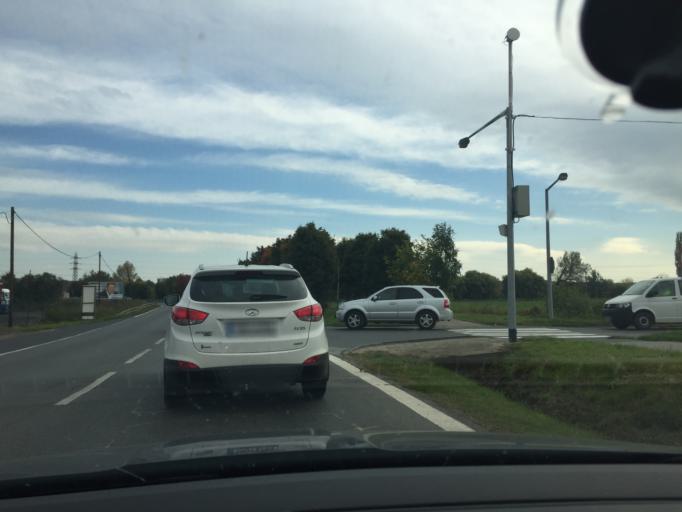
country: CZ
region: Praha
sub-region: Praha 20
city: Horni Pocernice
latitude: 50.0806
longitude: 14.6042
